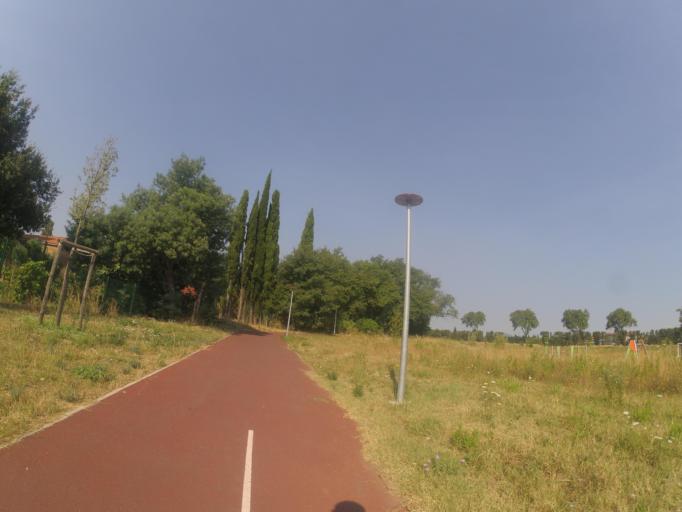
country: FR
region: Languedoc-Roussillon
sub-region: Departement des Pyrenees-Orientales
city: Toulouges
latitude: 42.6654
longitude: 2.8226
